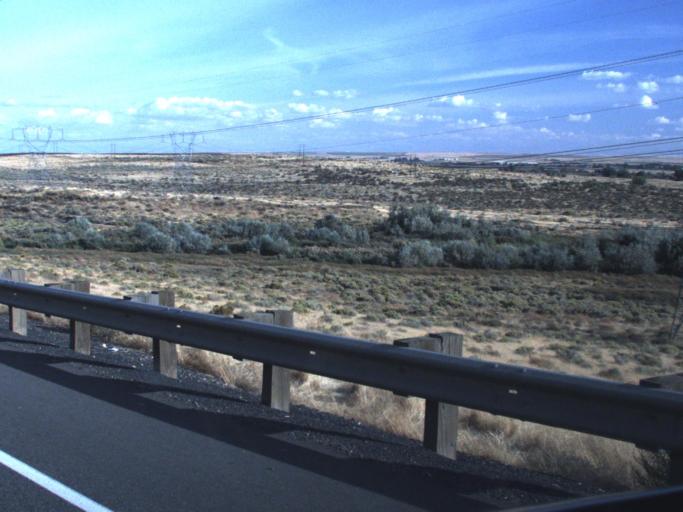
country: US
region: Oregon
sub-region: Morrow County
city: Irrigon
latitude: 45.9433
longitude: -119.5394
